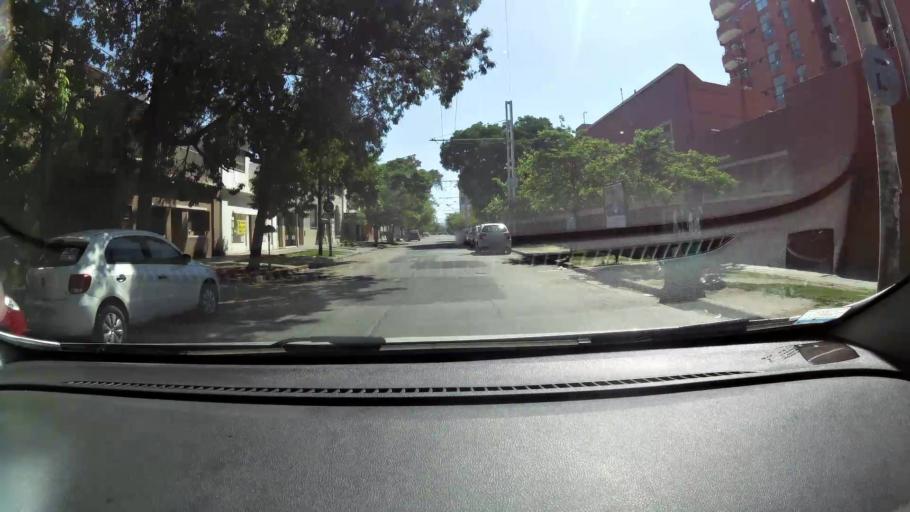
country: AR
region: Cordoba
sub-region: Departamento de Capital
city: Cordoba
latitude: -31.4096
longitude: -64.1638
